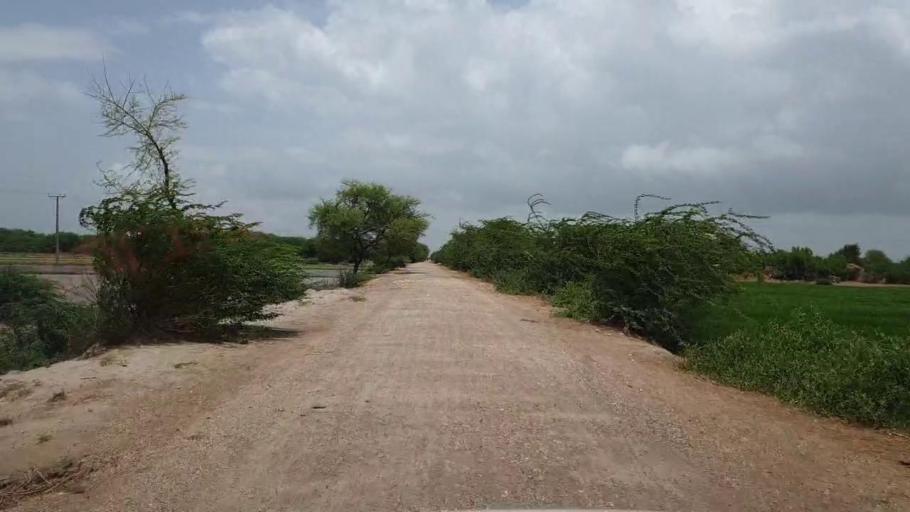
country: PK
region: Sindh
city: Kario
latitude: 24.6963
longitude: 68.6424
